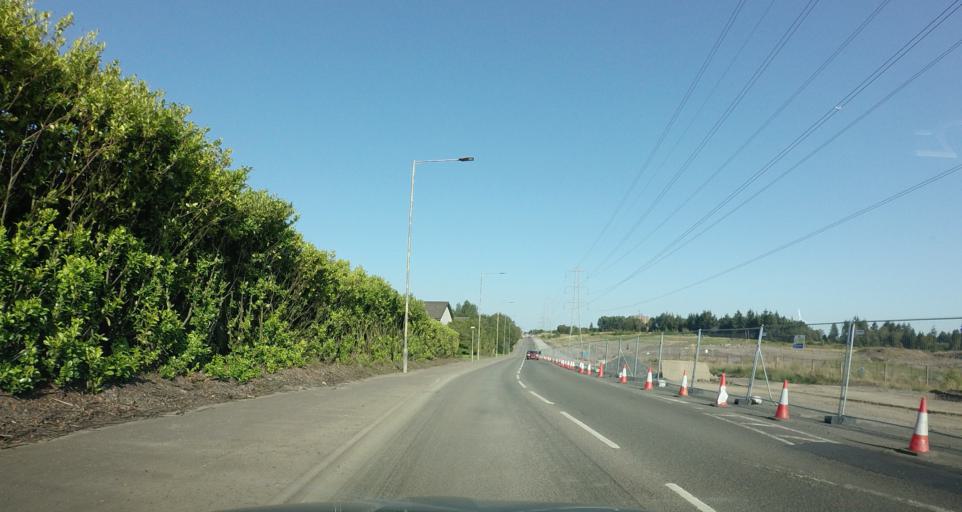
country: GB
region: Scotland
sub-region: South Lanarkshire
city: East Kilbride
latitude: 55.7412
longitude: -4.1822
